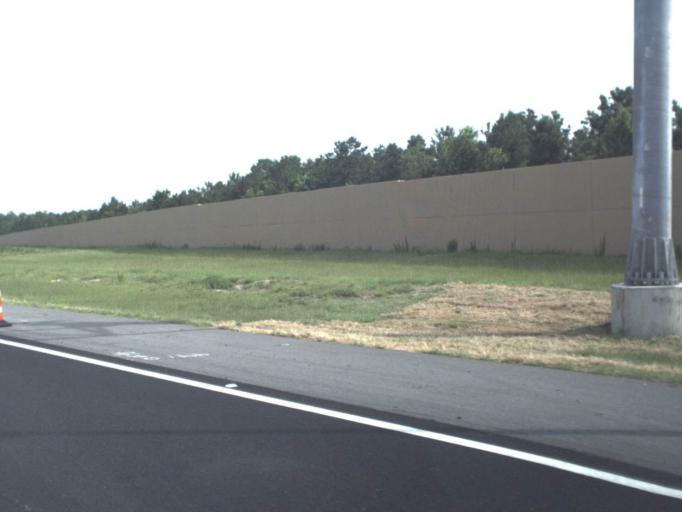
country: US
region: Florida
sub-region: Saint Johns County
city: Fruit Cove
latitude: 30.1096
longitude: -81.5089
